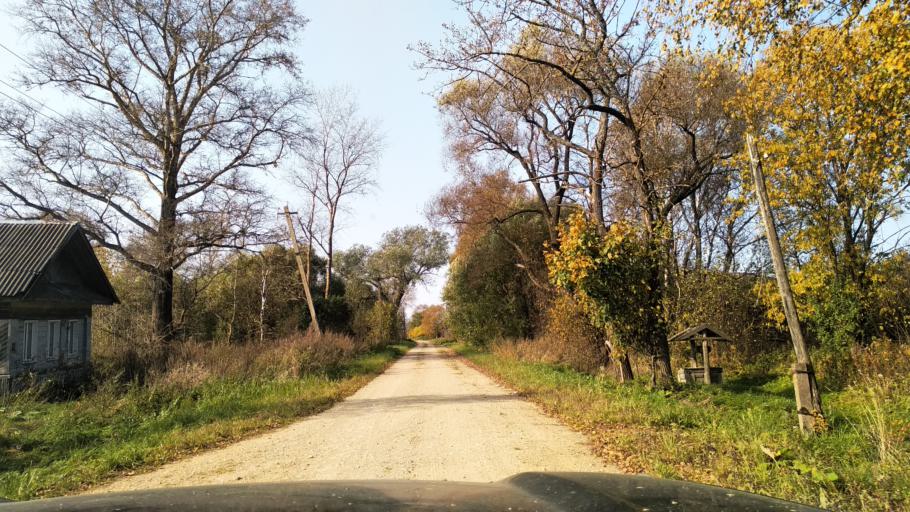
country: RU
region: Tverskaya
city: Krasnyy Kholm
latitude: 58.0334
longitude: 37.1807
